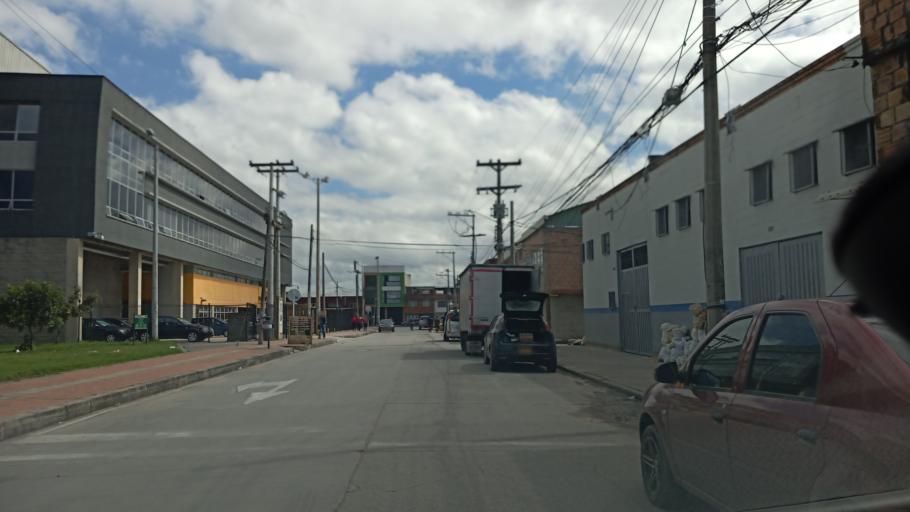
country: CO
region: Bogota D.C.
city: Bogota
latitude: 4.6833
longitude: -74.1279
